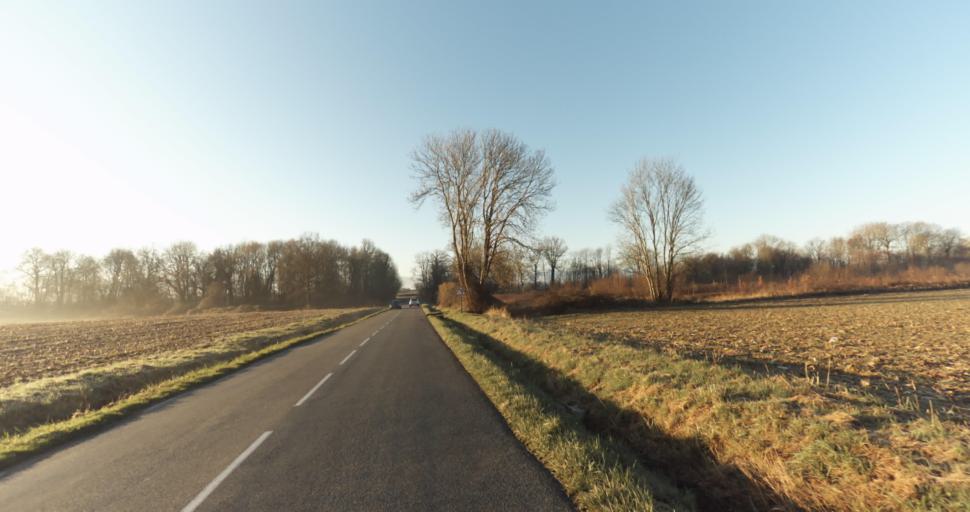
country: FR
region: Aquitaine
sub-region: Departement des Pyrenees-Atlantiques
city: Morlaas
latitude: 43.3223
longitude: -0.2741
